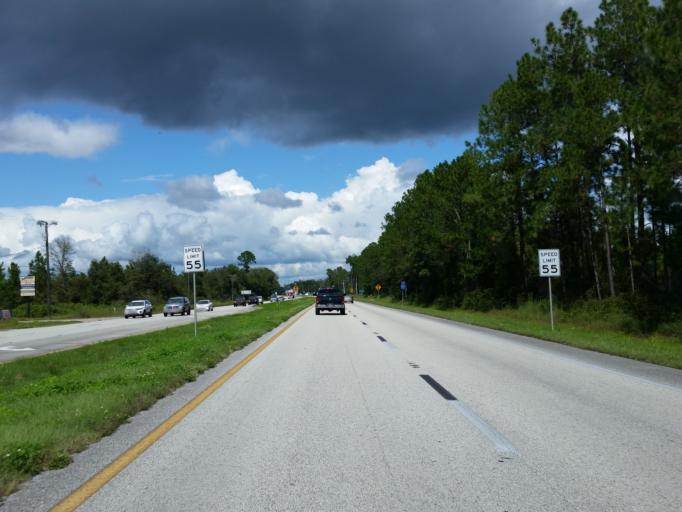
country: US
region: Florida
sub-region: Bradford County
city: Starke
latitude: 29.8964
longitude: -82.1379
